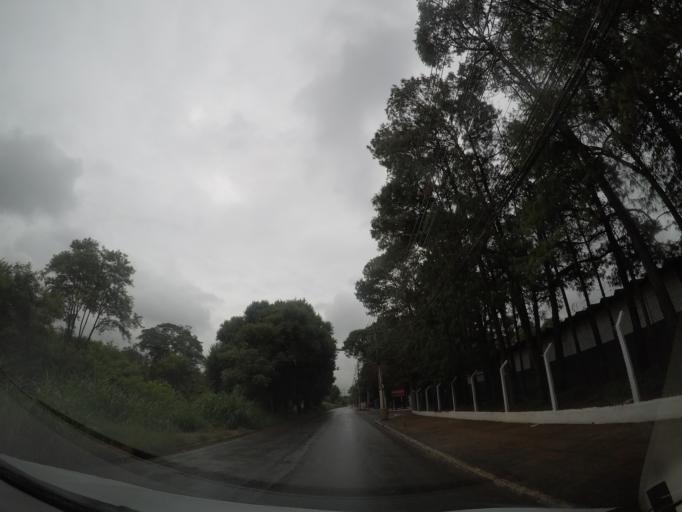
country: BR
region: Sao Paulo
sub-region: Guarulhos
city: Guarulhos
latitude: -23.4726
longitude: -46.4561
